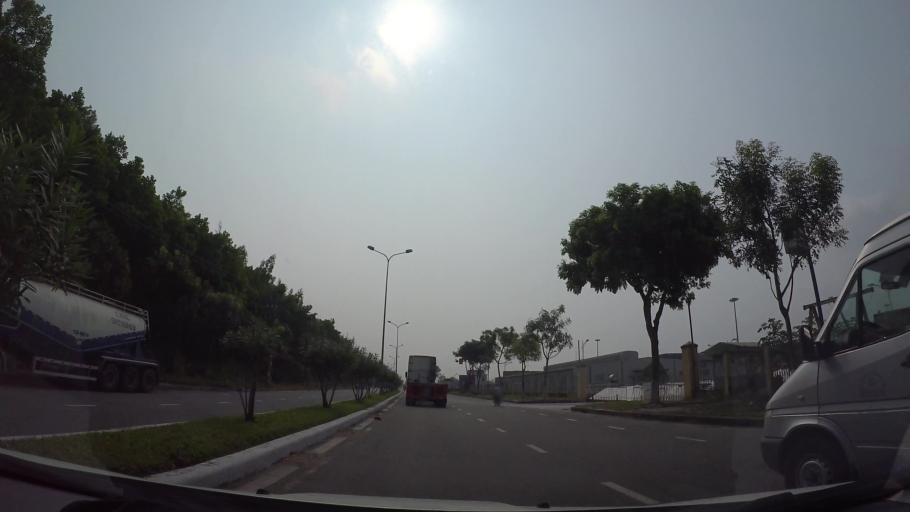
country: VN
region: Da Nang
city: Da Nang
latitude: 16.1177
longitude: 108.2300
